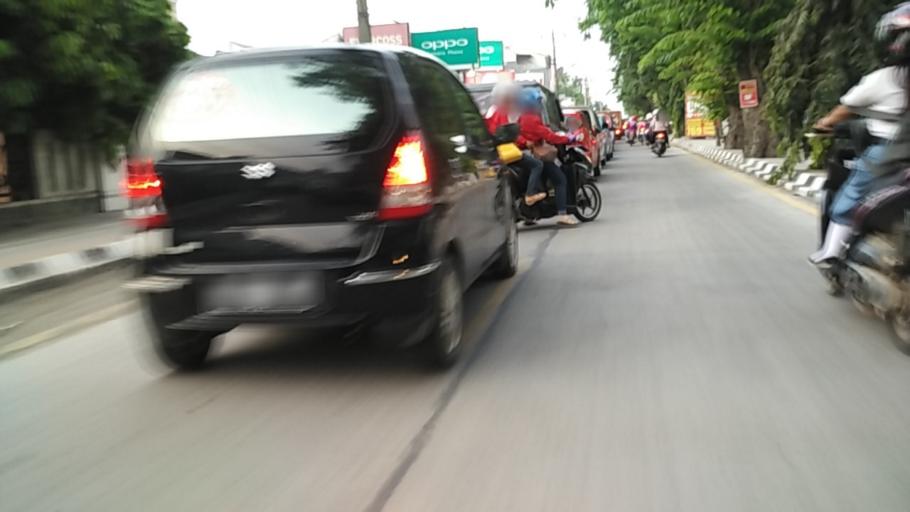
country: ID
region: Central Java
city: Semarang
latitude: -6.9812
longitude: 110.4602
